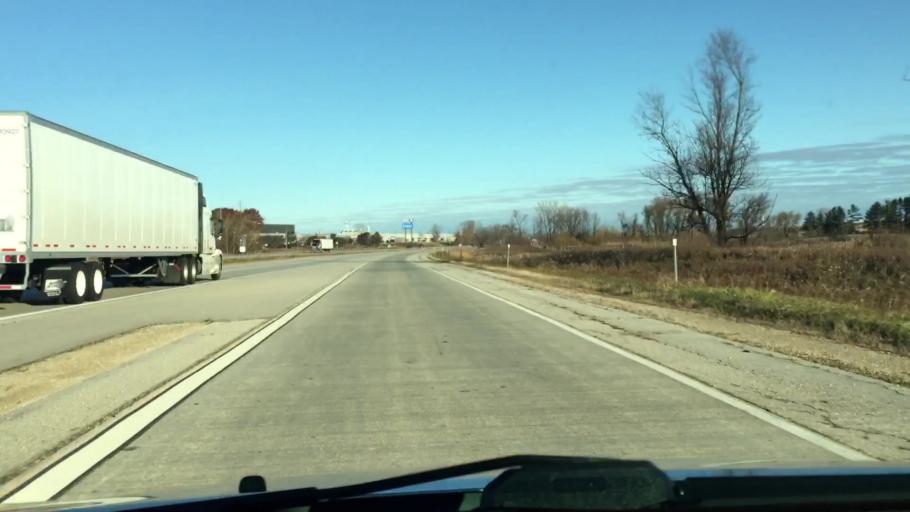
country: US
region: Wisconsin
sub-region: Dodge County
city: Lomira
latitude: 43.6197
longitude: -88.4389
